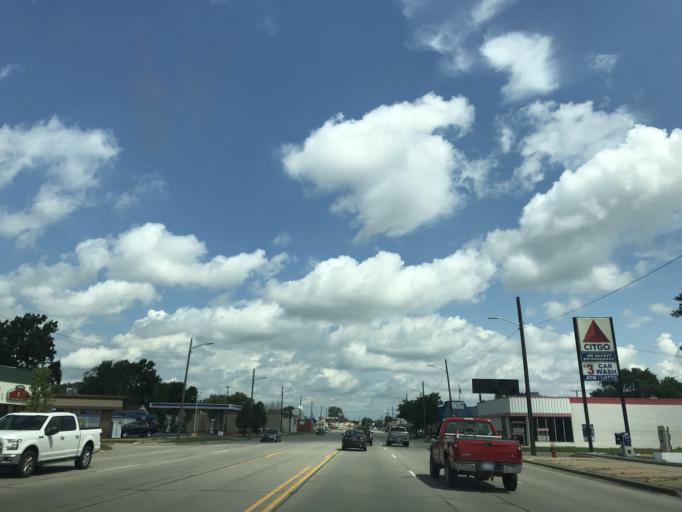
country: US
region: Michigan
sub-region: Wayne County
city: Lincoln Park
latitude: 42.2473
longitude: -83.1952
